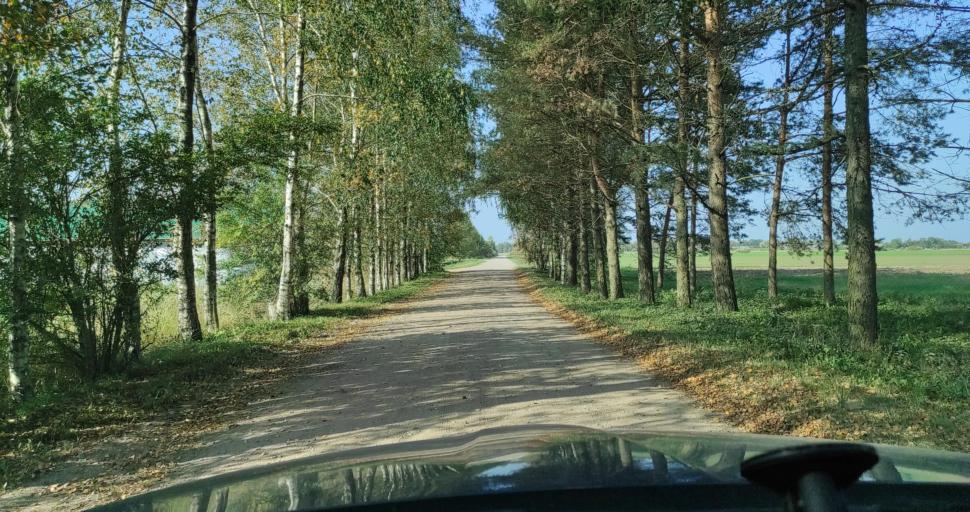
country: LV
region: Ventspils Rajons
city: Piltene
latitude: 57.2238
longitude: 21.6310
